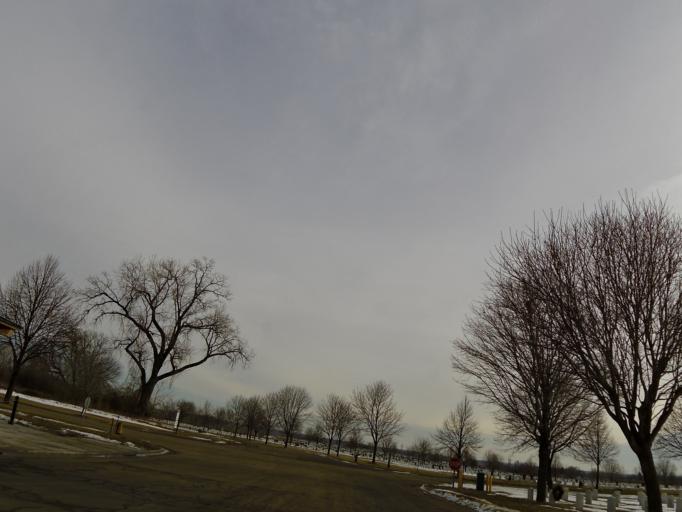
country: US
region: Minnesota
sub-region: Hennepin County
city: Richfield
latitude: 44.8691
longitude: -93.2144
